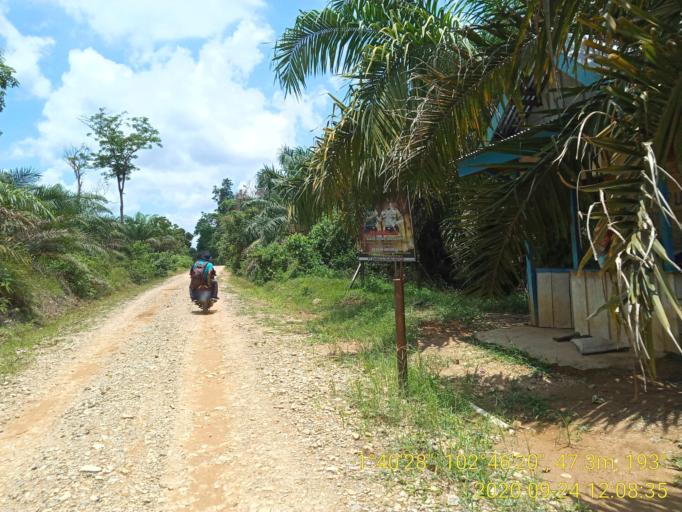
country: ID
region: Jambi
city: Sungaibengkal
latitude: -1.6745
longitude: 102.7724
